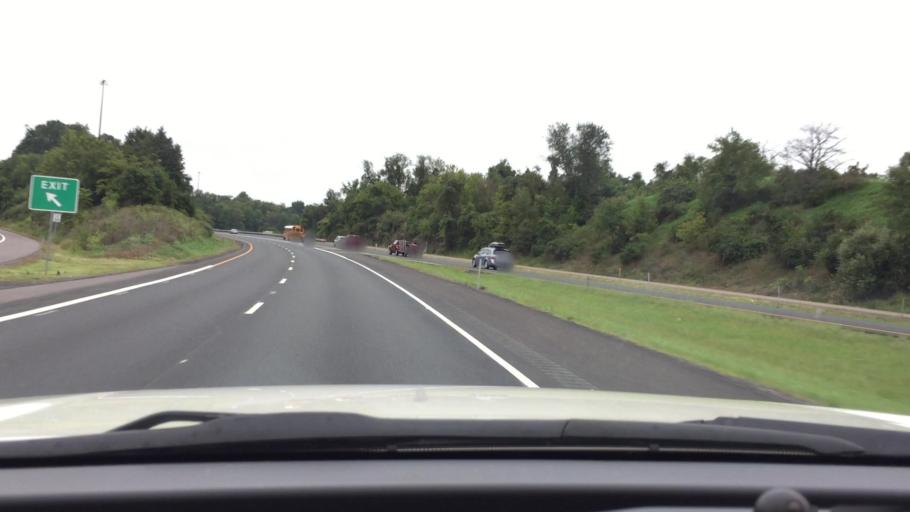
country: US
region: Maryland
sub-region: Washington County
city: Hancock
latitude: 39.7119
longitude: -78.1879
